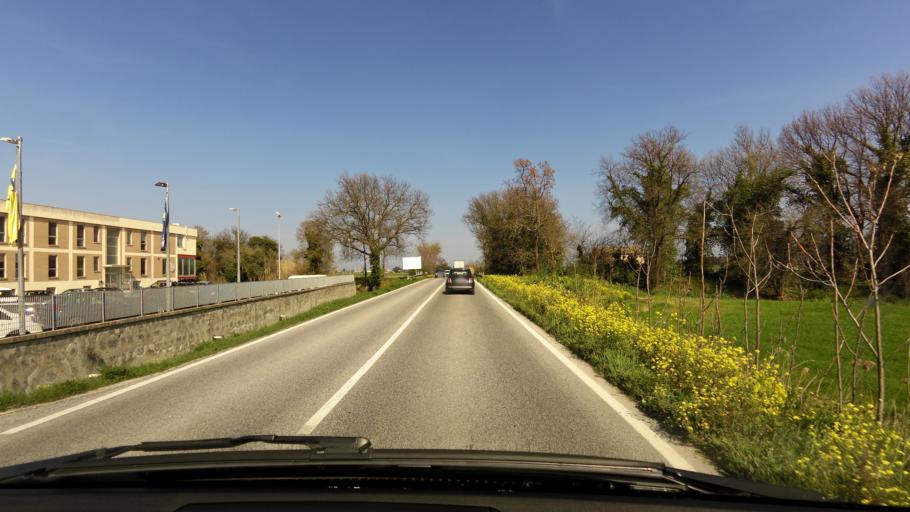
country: IT
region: The Marches
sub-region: Provincia di Macerata
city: Potenza Picena
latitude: 43.3819
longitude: 13.6127
